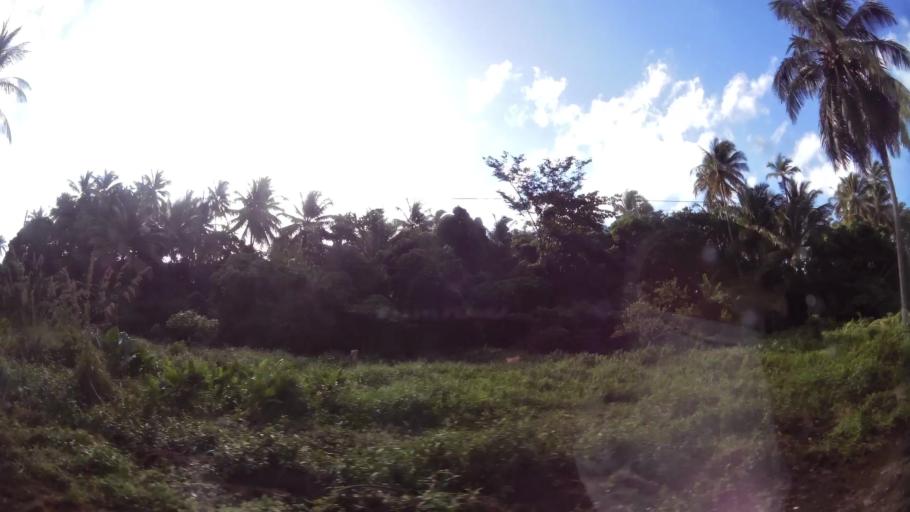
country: DM
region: Saint John
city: Portsmouth
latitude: 15.5761
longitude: -61.4484
